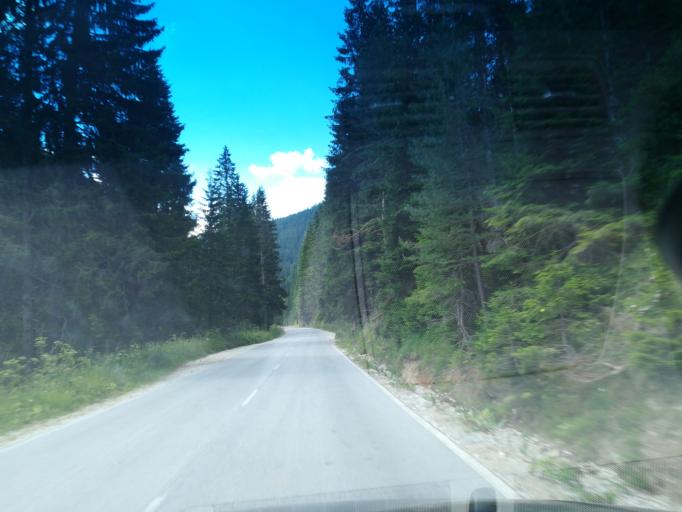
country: BG
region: Smolyan
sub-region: Obshtina Smolyan
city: Smolyan
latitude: 41.6588
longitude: 24.6827
